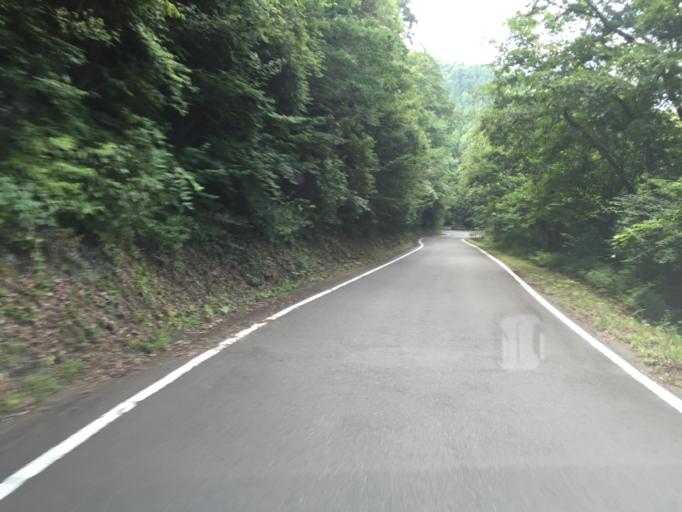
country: JP
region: Fukushima
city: Inawashiro
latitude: 37.4159
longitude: 140.1030
